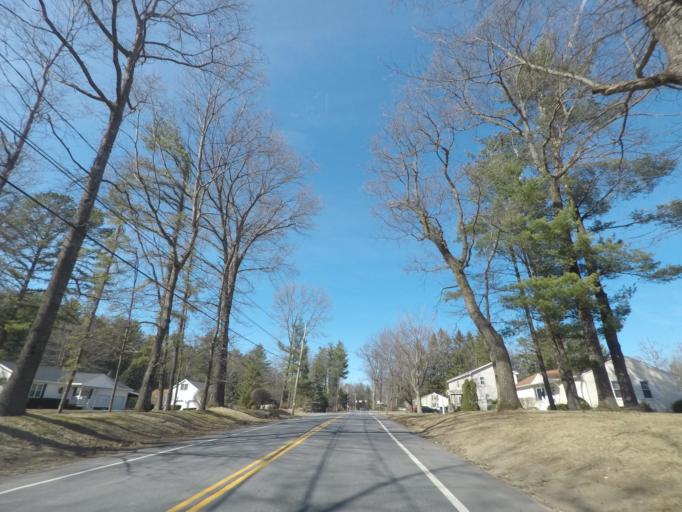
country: US
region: New York
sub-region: Saratoga County
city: North Ballston Spa
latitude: 43.0217
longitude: -73.8487
